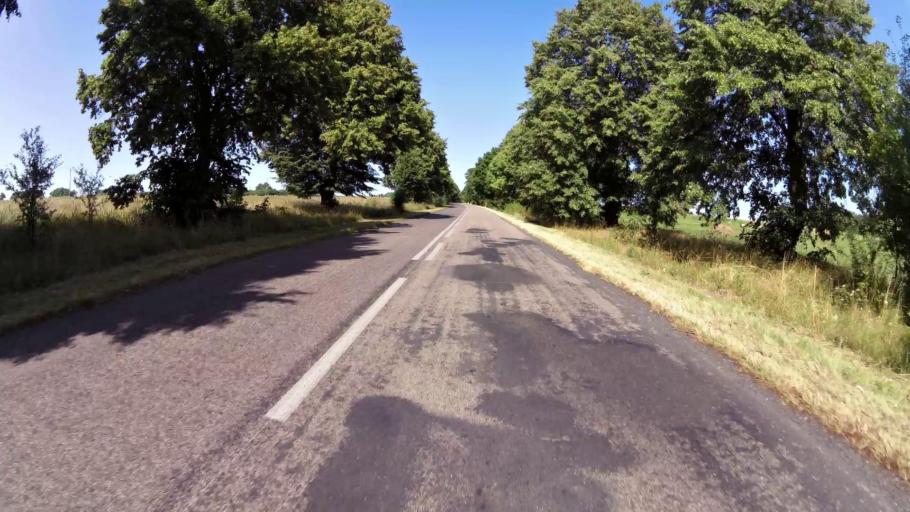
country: PL
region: West Pomeranian Voivodeship
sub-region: Powiat stargardzki
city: Dobrzany
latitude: 53.3253
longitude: 15.3892
